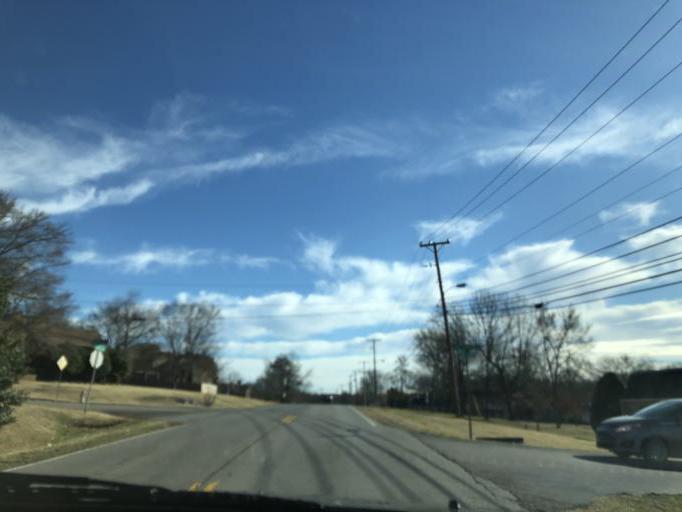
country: US
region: Tennessee
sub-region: Wilson County
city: Green Hill
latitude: 36.1611
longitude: -86.5911
